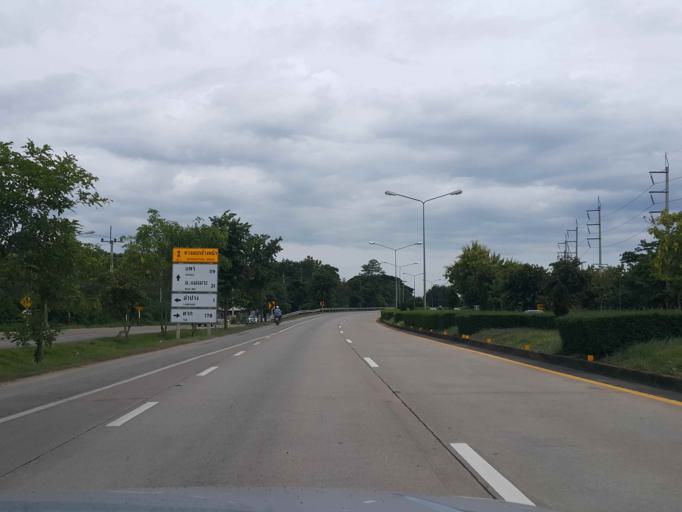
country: TH
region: Lampang
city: Lampang
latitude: 18.2724
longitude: 99.4613
